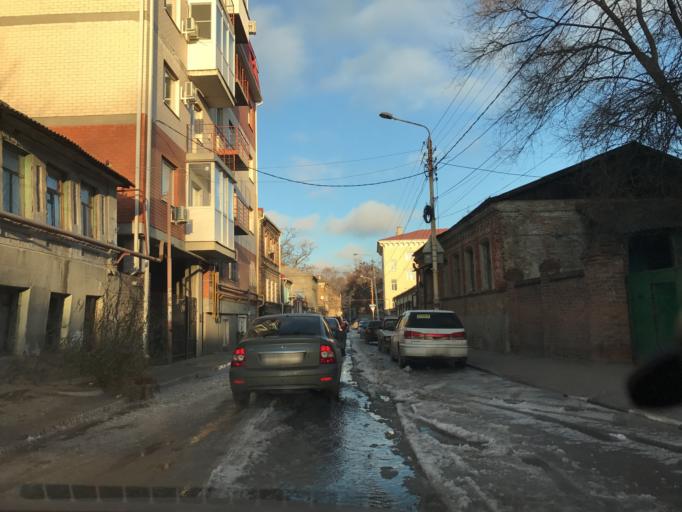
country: RU
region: Rostov
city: Rostov-na-Donu
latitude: 47.2177
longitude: 39.6856
